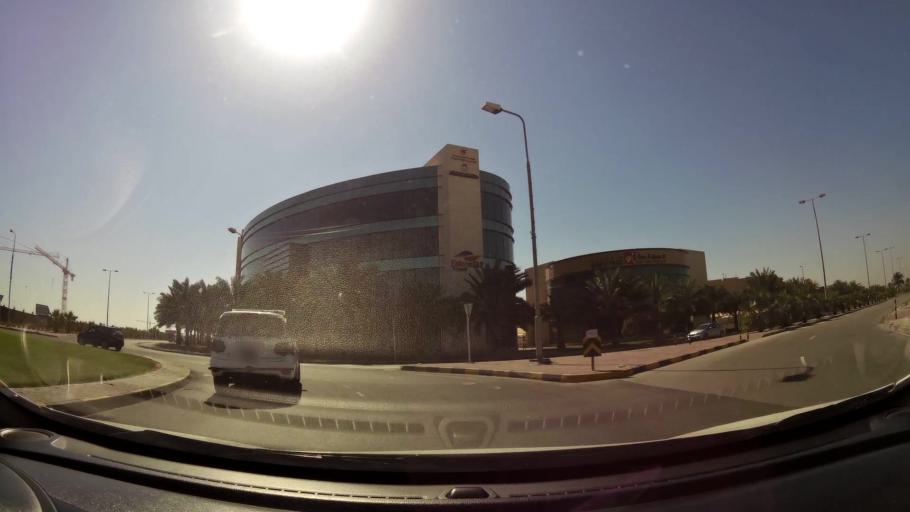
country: BH
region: Muharraq
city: Al Muharraq
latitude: 26.2667
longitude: 50.6260
